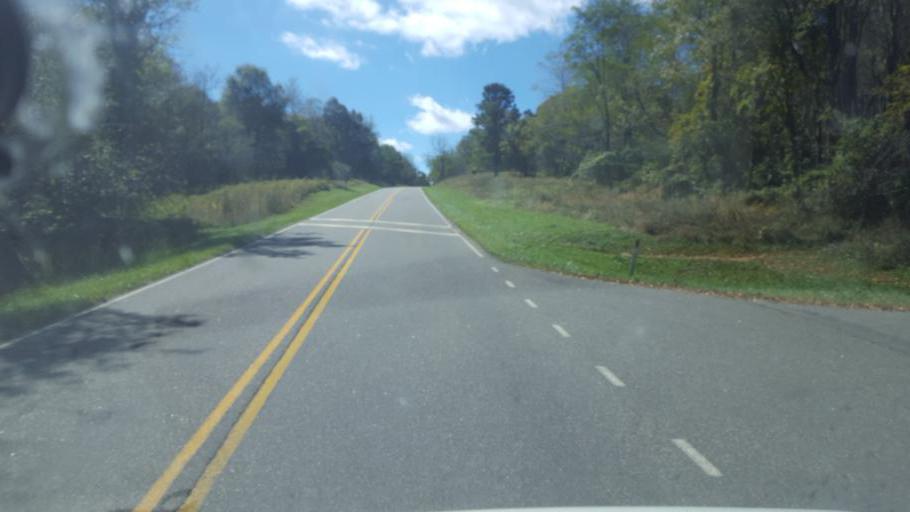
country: US
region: Virginia
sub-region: Page County
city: Stanley
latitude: 38.4999
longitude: -78.4456
